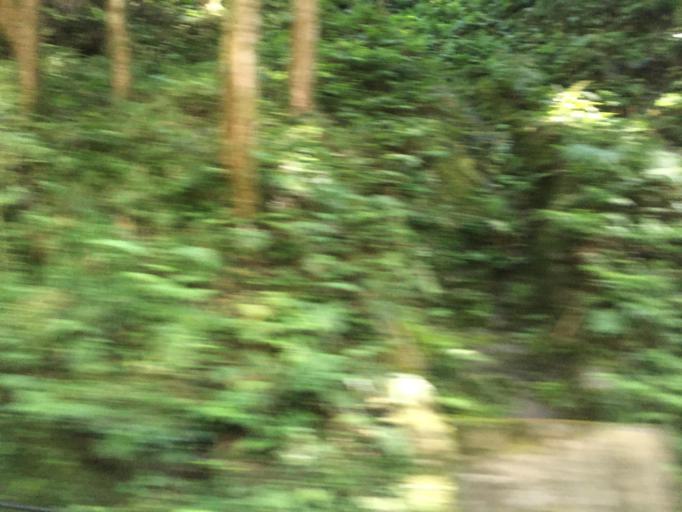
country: TW
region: Taiwan
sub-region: Yilan
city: Yilan
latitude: 24.6216
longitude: 121.4794
